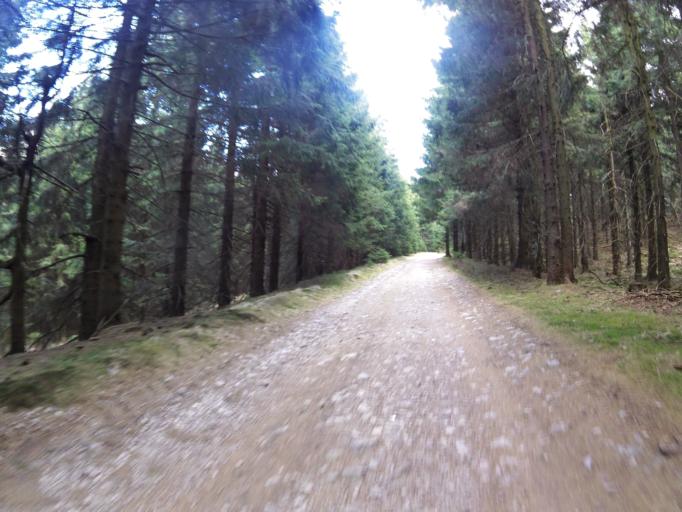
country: DE
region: Thuringia
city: Bermbach
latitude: 50.7283
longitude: 10.6412
